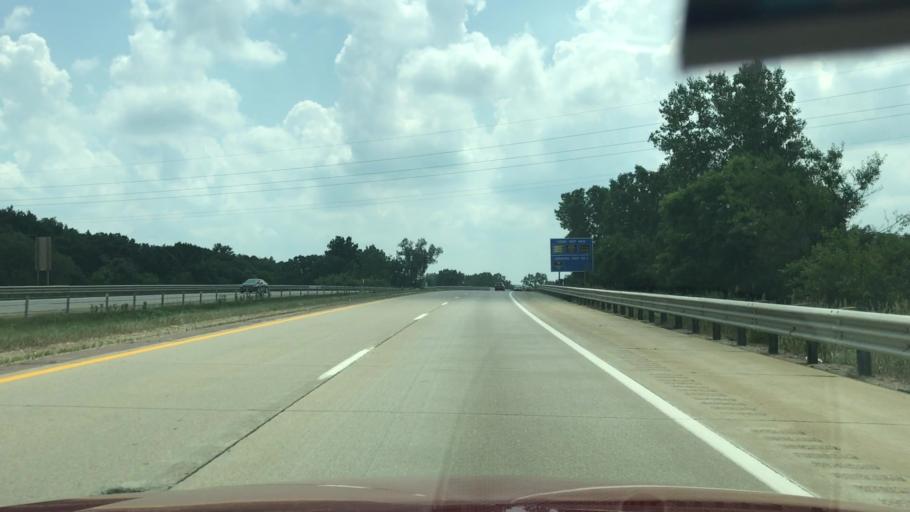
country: US
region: Michigan
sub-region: Allegan County
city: Plainwell
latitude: 42.4610
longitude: -85.6527
